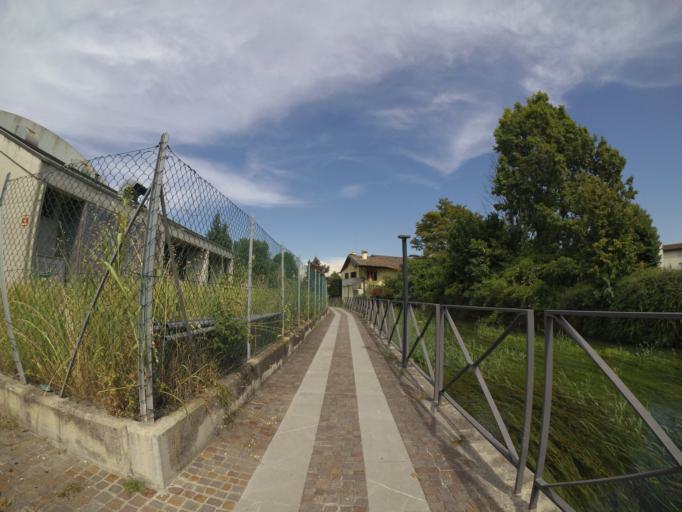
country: IT
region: Friuli Venezia Giulia
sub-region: Provincia di Udine
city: Camino al Tagliamento
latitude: 45.9268
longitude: 12.9425
